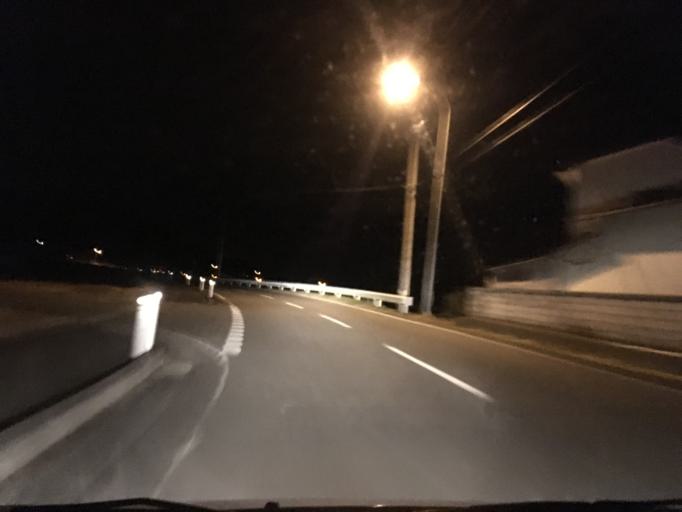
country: JP
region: Iwate
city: Ichinoseki
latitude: 38.7495
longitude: 141.2263
